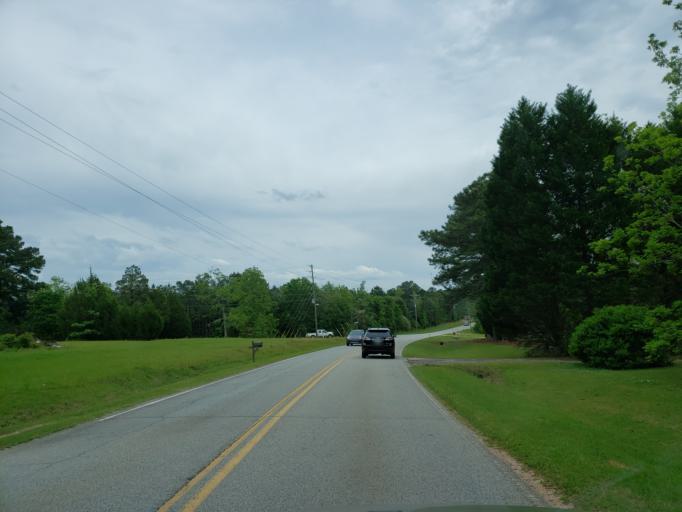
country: US
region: Georgia
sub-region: Bibb County
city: West Point
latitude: 32.8151
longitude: -83.8527
